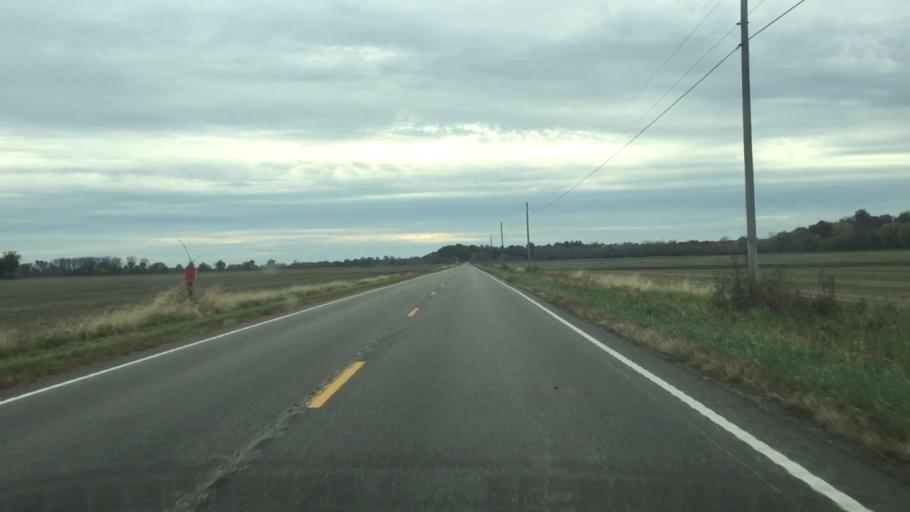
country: US
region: Missouri
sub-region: Callaway County
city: Fulton
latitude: 38.7035
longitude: -91.8064
